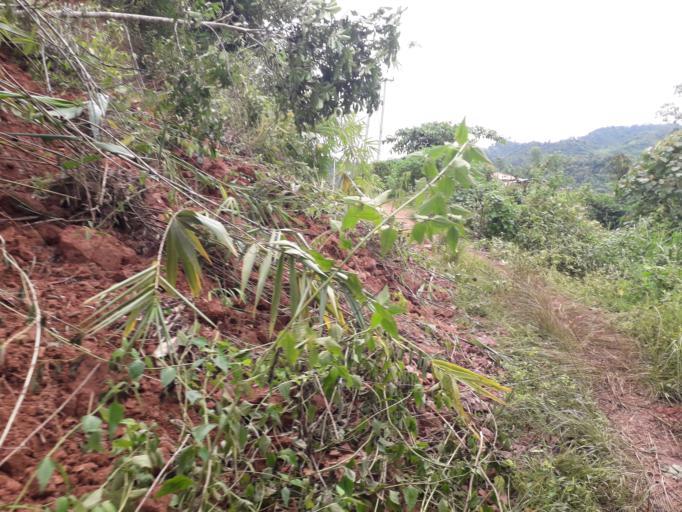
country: CN
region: Yunnan
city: Menglie
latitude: 22.2076
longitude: 101.6645
